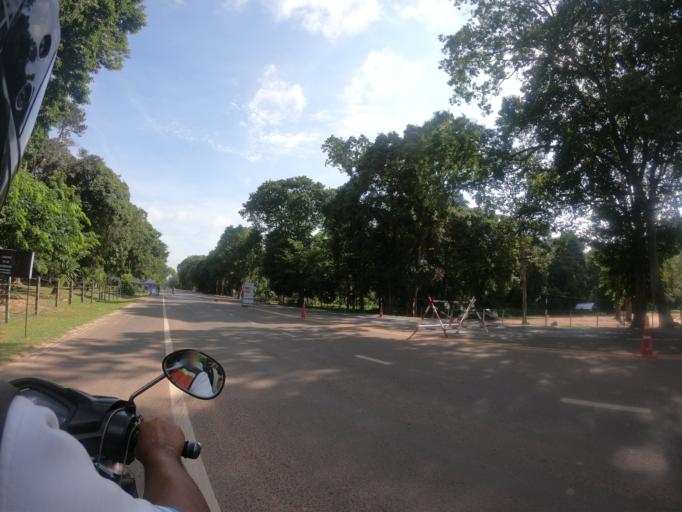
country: TH
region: Surin
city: Kap Choeng
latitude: 14.4410
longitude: 103.7007
